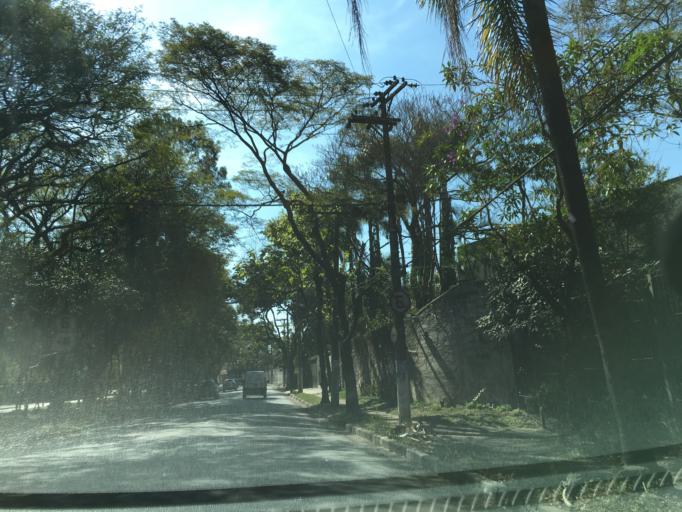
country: BR
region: Sao Paulo
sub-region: Sao Paulo
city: Sao Paulo
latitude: -23.5658
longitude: -46.7071
